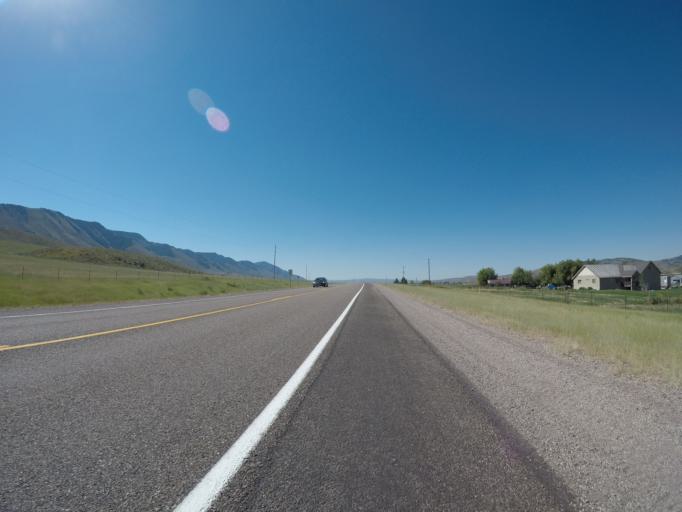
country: US
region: Idaho
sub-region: Bear Lake County
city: Montpelier
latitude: 42.3726
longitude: -111.0533
